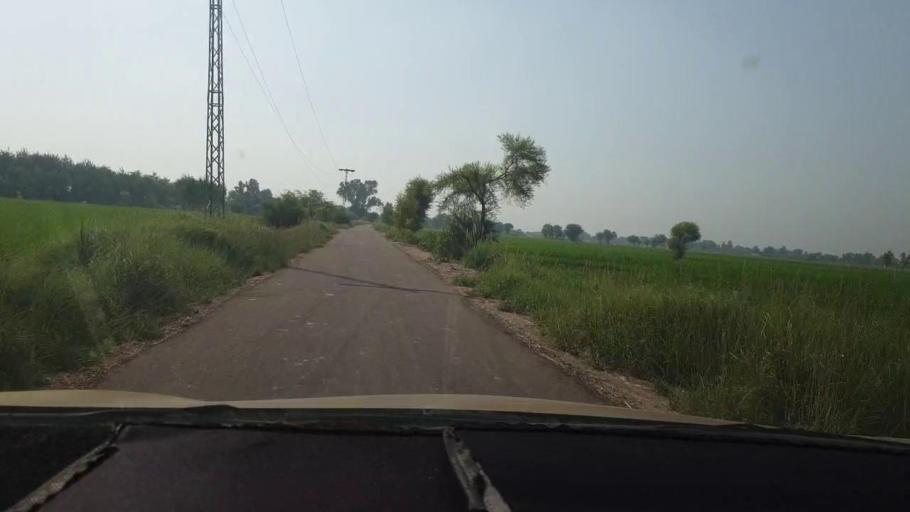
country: PK
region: Sindh
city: Kambar
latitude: 27.5817
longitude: 68.0720
